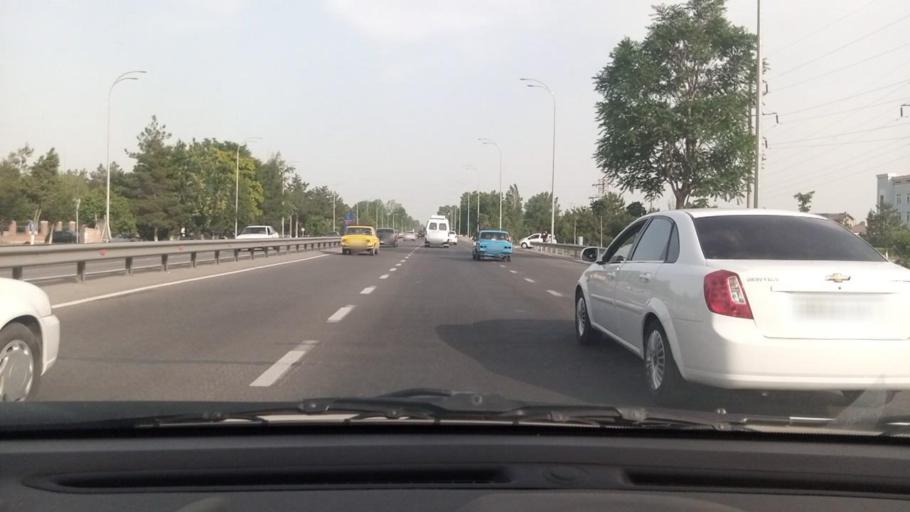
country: UZ
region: Toshkent Shahri
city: Bektemir
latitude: 41.2556
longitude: 69.3822
